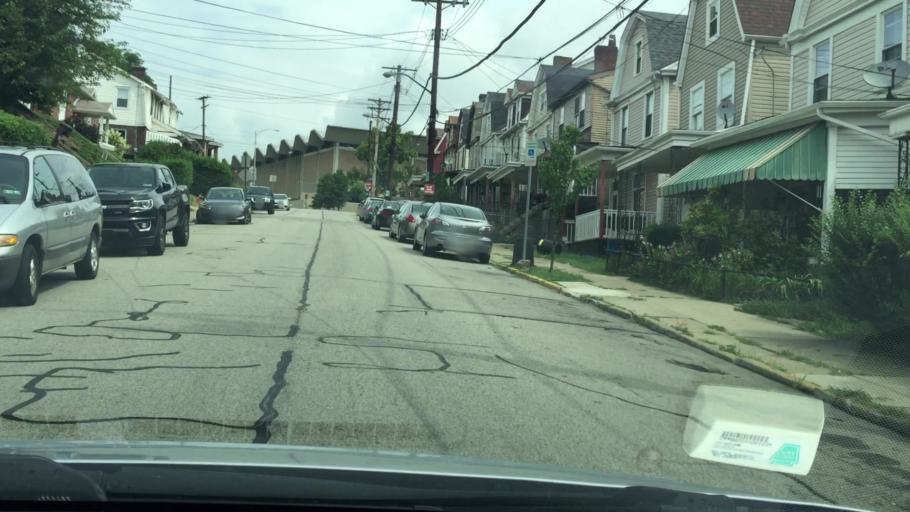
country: US
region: Pennsylvania
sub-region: Allegheny County
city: Bloomfield
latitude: 40.4418
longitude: -79.9657
